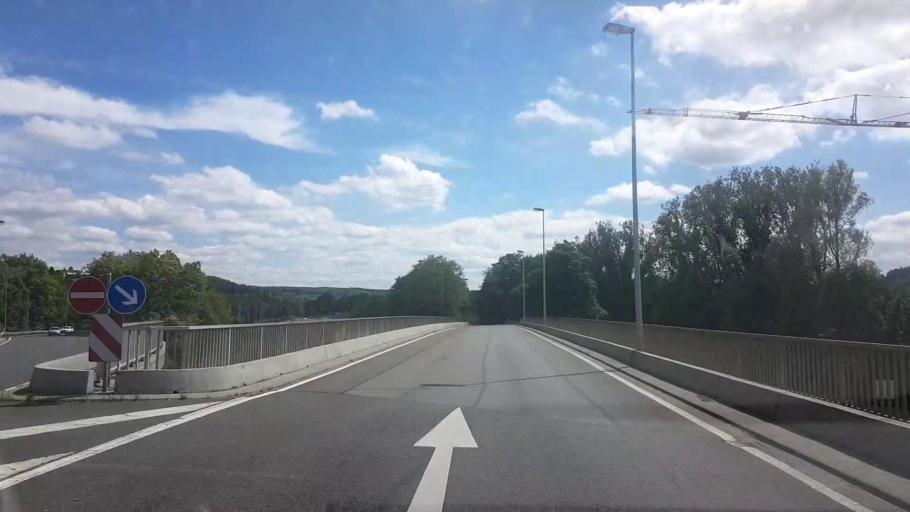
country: DE
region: Bavaria
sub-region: Upper Franconia
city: Coburg
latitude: 50.2416
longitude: 10.9710
